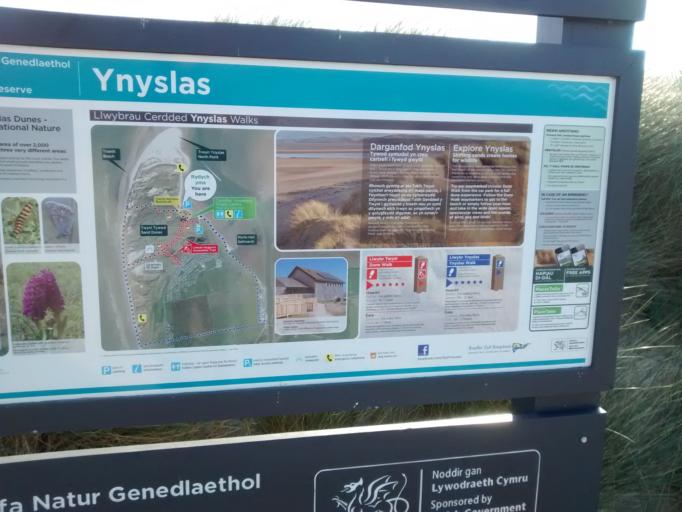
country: GB
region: Wales
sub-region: Gwynedd
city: Tywyn
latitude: 52.5278
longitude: -4.0518
